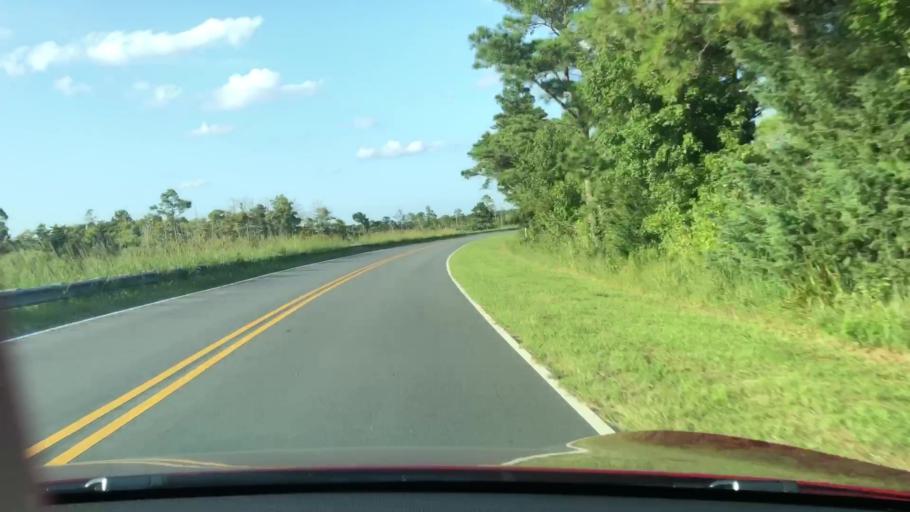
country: US
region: North Carolina
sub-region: Dare County
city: Wanchese
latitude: 35.6913
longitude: -75.7807
